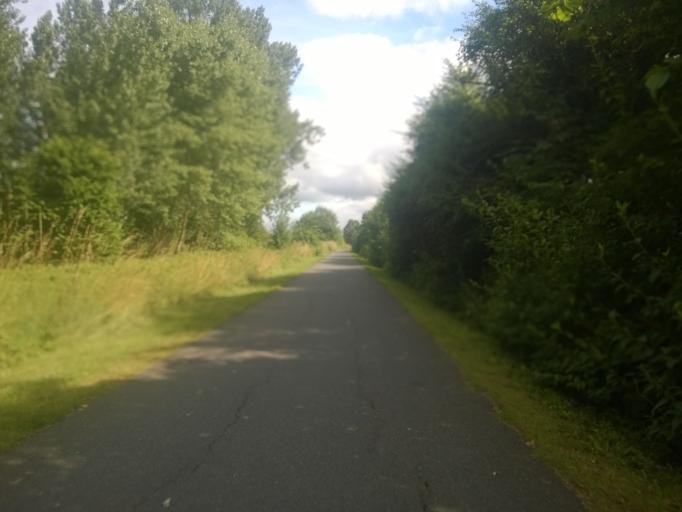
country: SE
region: Skane
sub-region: Kristianstads Kommun
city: Kristianstad
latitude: 56.0495
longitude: 14.1671
